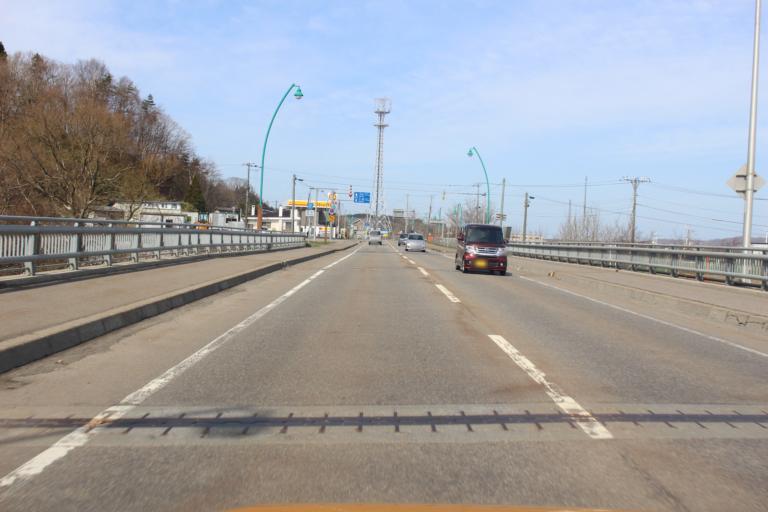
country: JP
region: Hokkaido
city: Kamiiso
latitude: 41.9172
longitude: 140.2220
